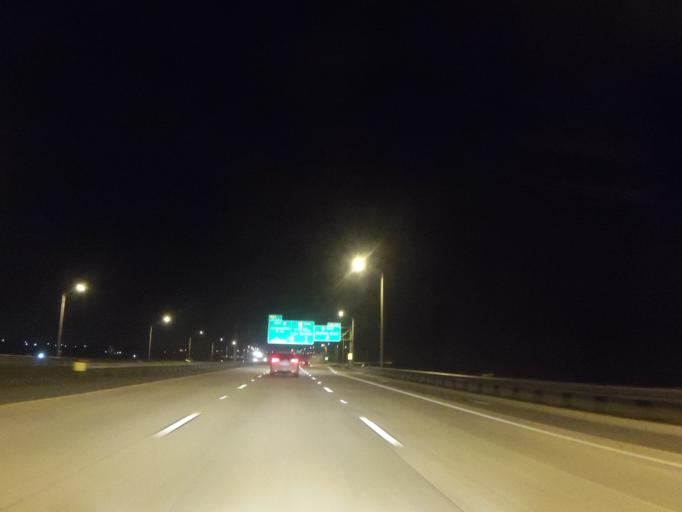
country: US
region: Florida
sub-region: Saint Johns County
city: Fruit Cove
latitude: 30.1046
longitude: -81.5162
